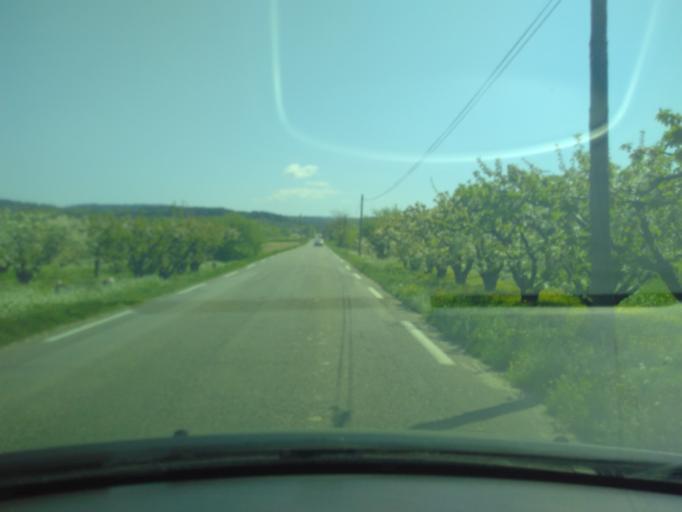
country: FR
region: Provence-Alpes-Cote d'Azur
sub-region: Departement du Vaucluse
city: Malemort-du-Comtat
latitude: 44.0233
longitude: 5.1453
